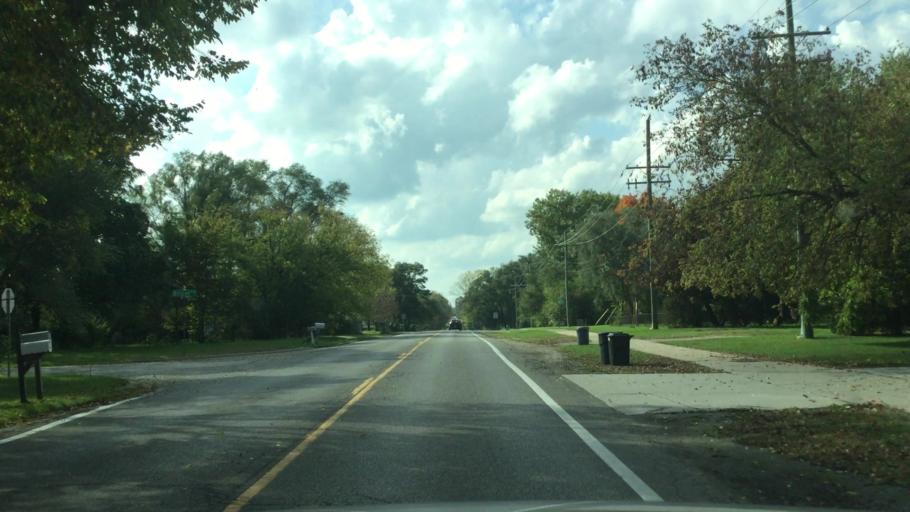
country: US
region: Michigan
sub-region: Oakland County
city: Waterford
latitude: 42.6530
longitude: -83.3910
